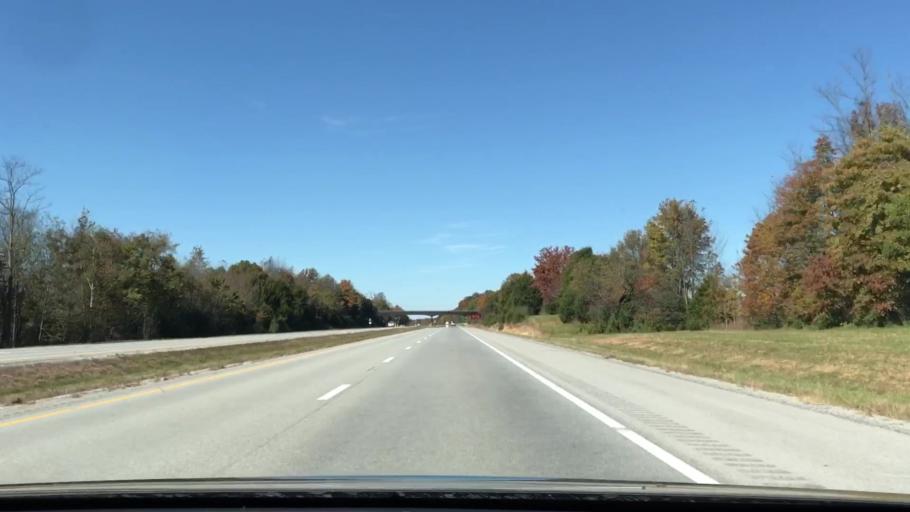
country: US
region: Kentucky
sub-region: Barren County
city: Cave City
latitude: 37.0351
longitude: -86.0564
